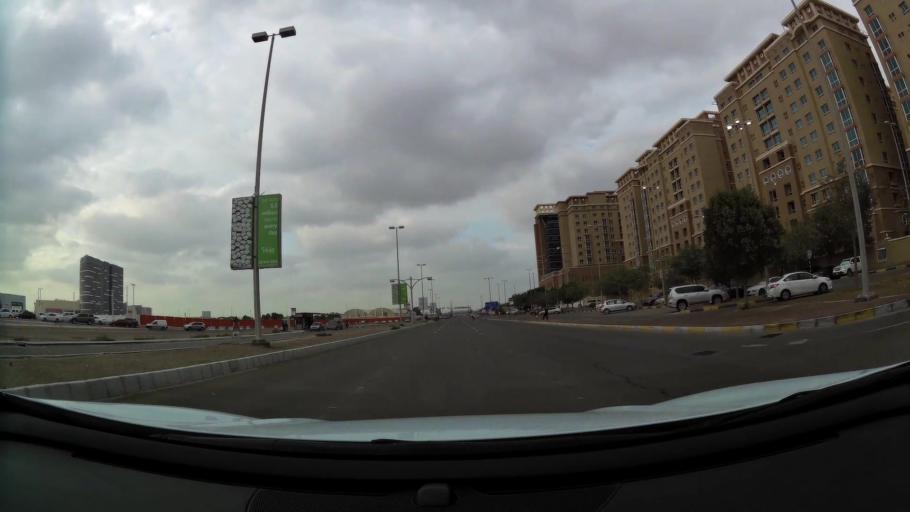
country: AE
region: Abu Dhabi
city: Abu Dhabi
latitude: 24.3711
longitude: 54.5365
